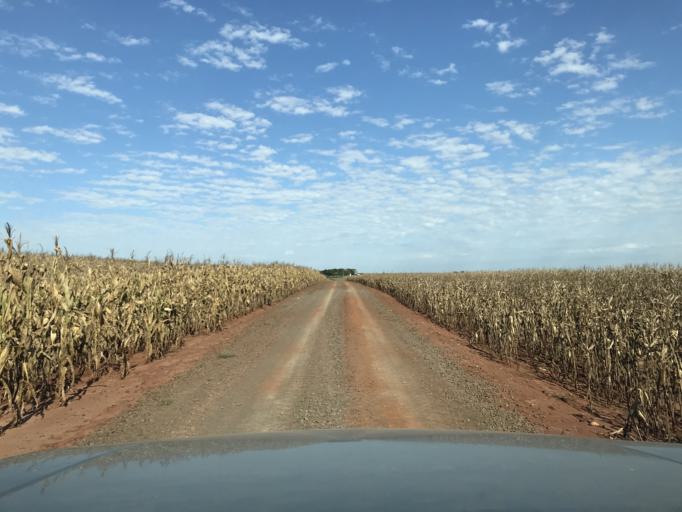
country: BR
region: Parana
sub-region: Palotina
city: Palotina
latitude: -24.1688
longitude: -53.7558
